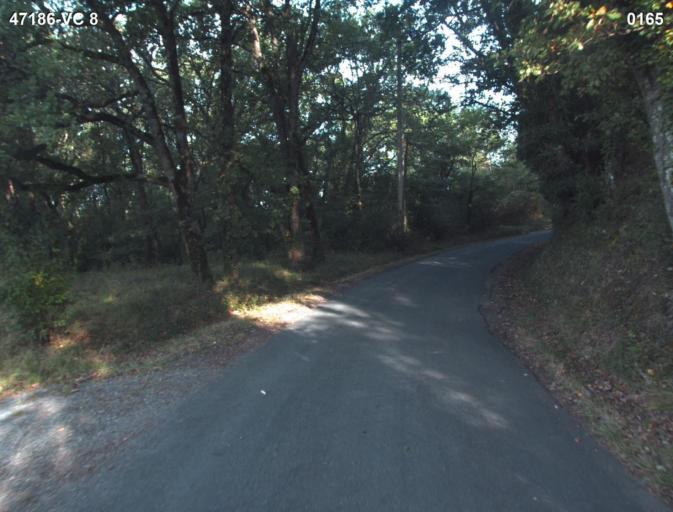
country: FR
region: Aquitaine
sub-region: Departement du Lot-et-Garonne
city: Port-Sainte-Marie
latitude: 44.1850
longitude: 0.4247
